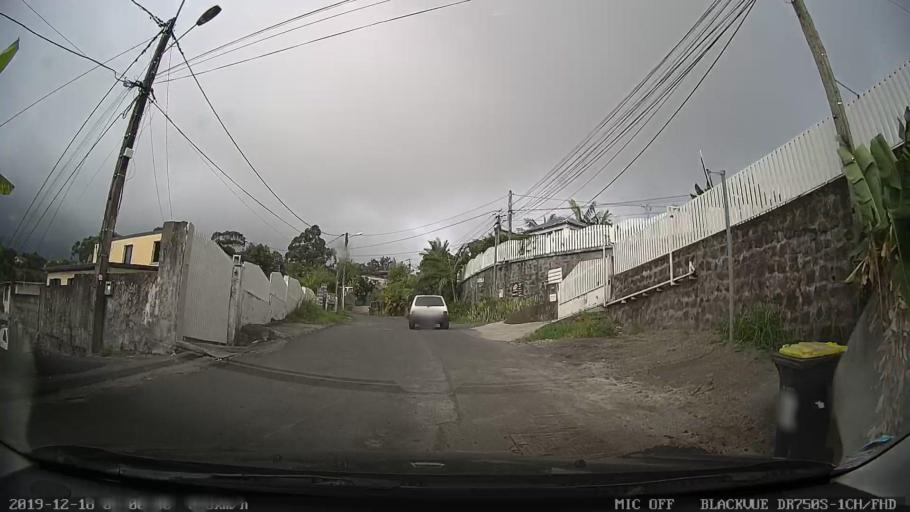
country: RE
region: Reunion
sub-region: Reunion
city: Le Tampon
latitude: -21.2544
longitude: 55.5171
